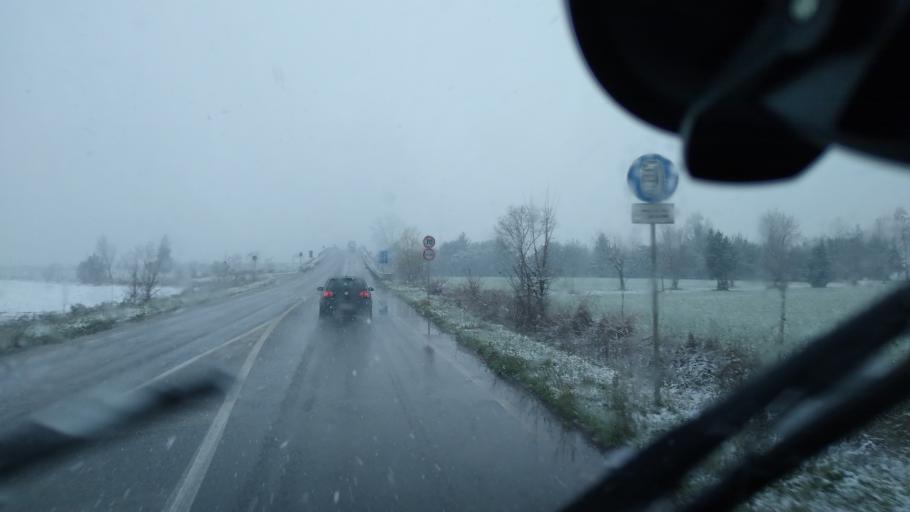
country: IT
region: Lombardy
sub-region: Provincia di Bergamo
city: Bariano
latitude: 45.5098
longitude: 9.6988
